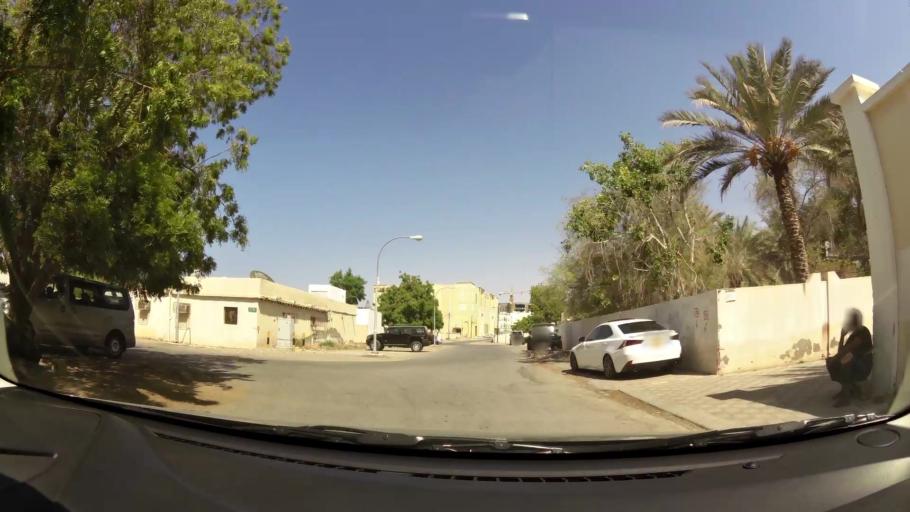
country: OM
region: Muhafazat Masqat
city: As Sib al Jadidah
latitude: 23.6413
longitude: 58.2215
